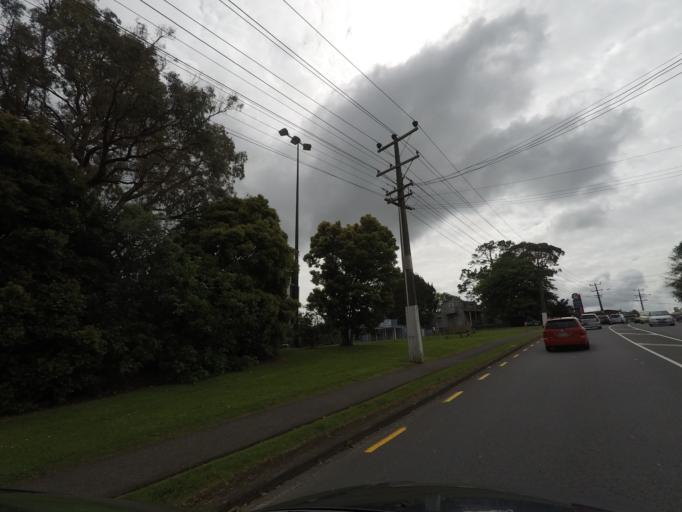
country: NZ
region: Auckland
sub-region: Auckland
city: Waitakere
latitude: -36.9084
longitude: 174.6449
